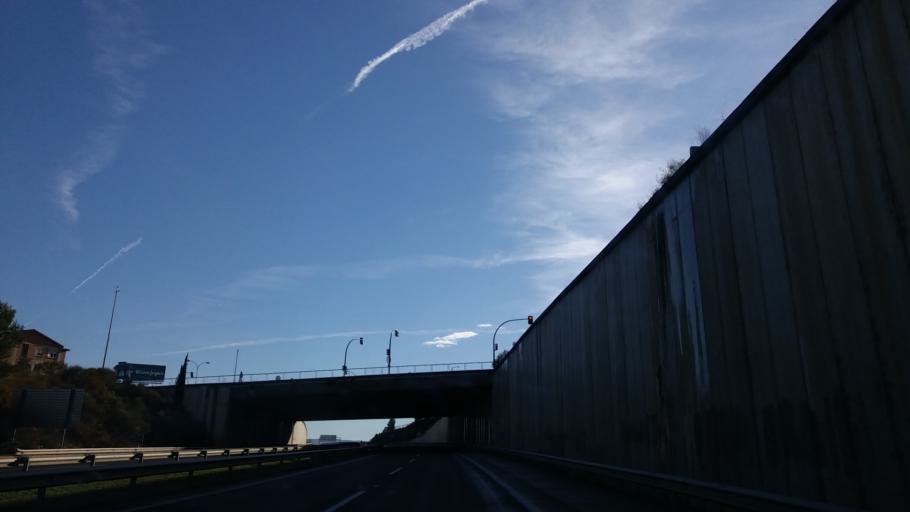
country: ES
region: Navarre
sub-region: Provincia de Navarra
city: Cizur Mayor
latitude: 42.7937
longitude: -1.6852
